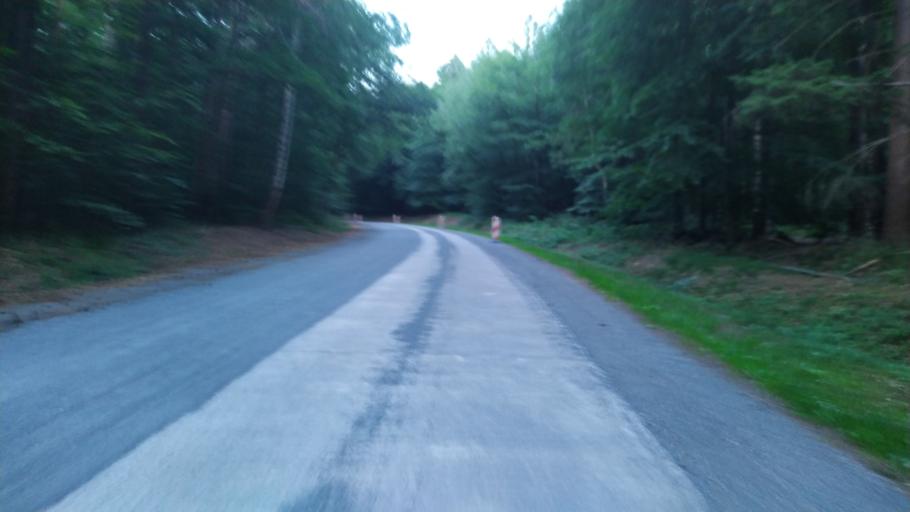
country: DE
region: Lower Saxony
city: Bremervorde
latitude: 53.4909
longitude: 9.2175
